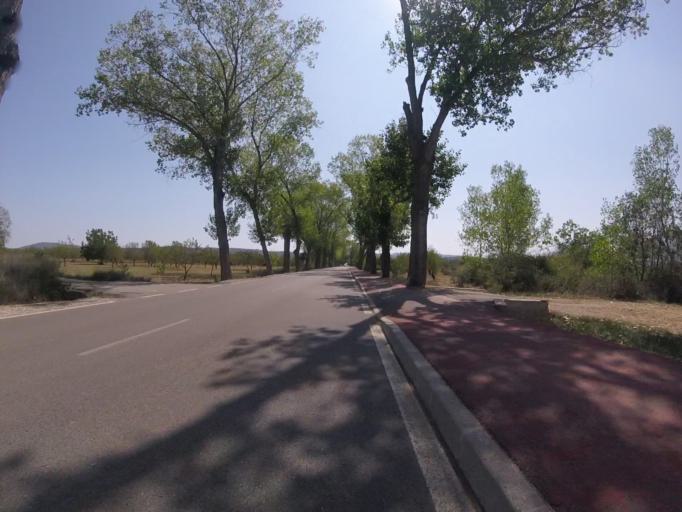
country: ES
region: Valencia
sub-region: Provincia de Castello
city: Cabanes
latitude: 40.1634
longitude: 0.0208
